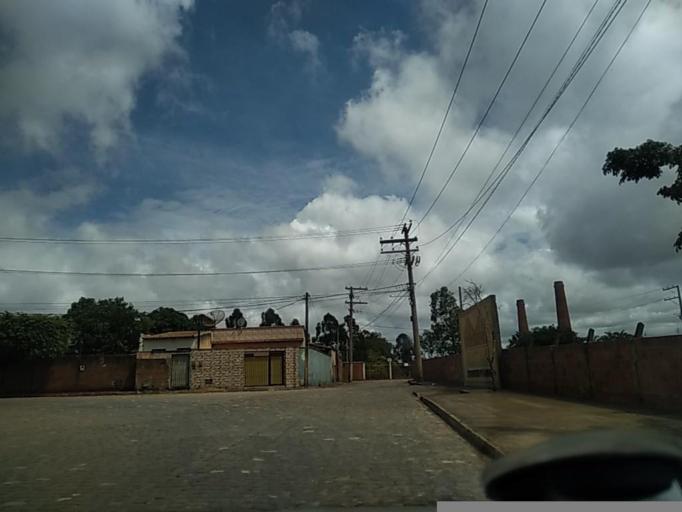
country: BR
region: Bahia
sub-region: Caetite
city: Caetite
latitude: -14.0541
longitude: -42.4838
